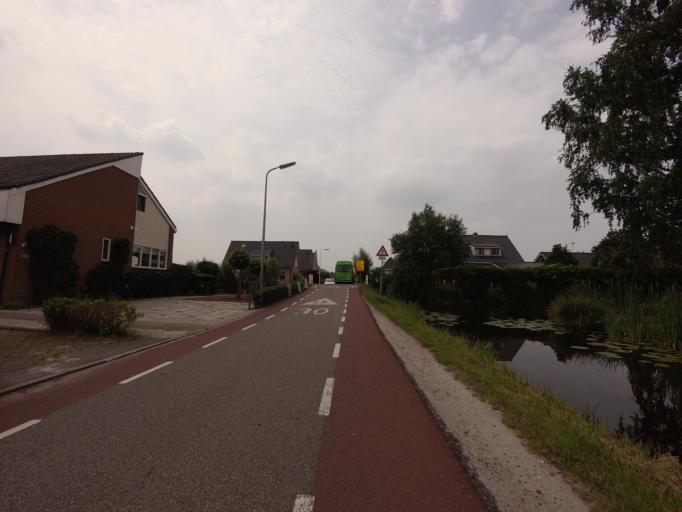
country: NL
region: South Holland
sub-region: Molenwaard
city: Nieuw-Lekkerland
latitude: 51.9473
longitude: 4.7054
